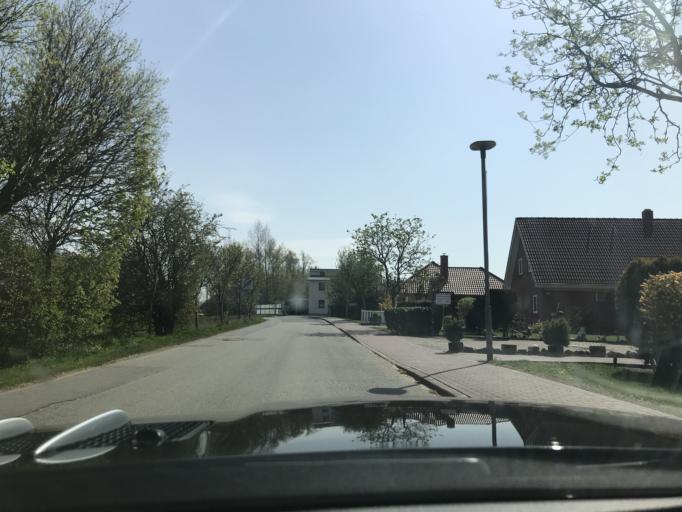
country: DE
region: Schleswig-Holstein
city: Grossenbrode
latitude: 54.3656
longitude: 11.0893
